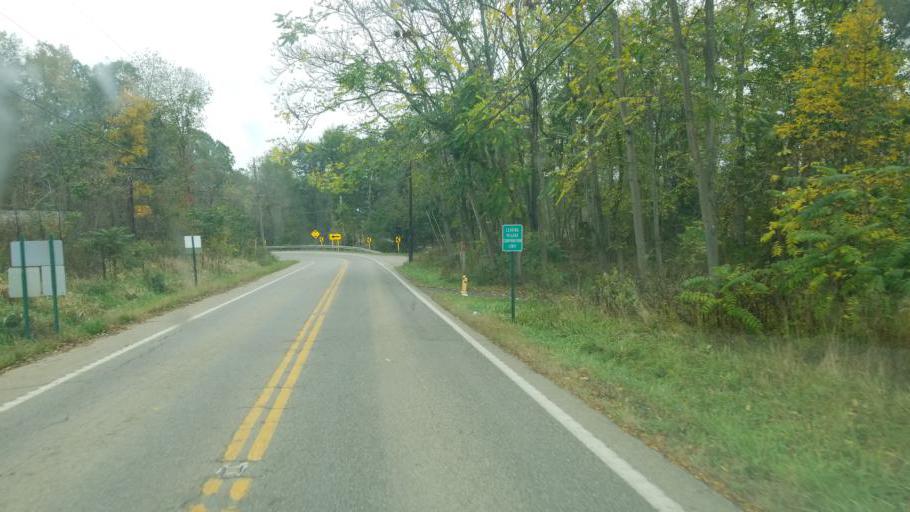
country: US
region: Ohio
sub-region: Tuscarawas County
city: Strasburg
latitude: 40.6549
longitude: -81.4644
